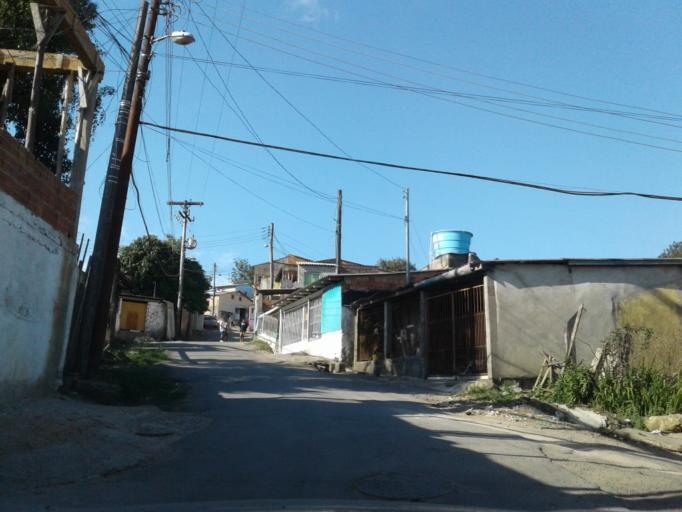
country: BR
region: Rio Grande do Sul
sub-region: Porto Alegre
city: Porto Alegre
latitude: -30.0465
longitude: -51.1530
